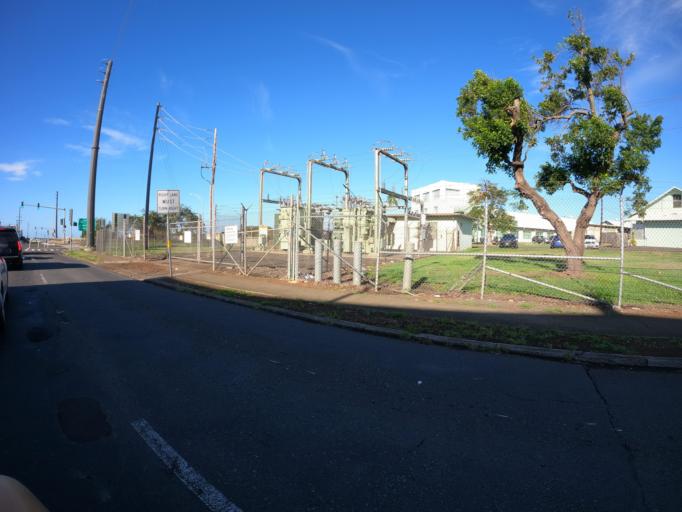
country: US
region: Hawaii
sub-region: Honolulu County
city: Honolulu
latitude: 21.3384
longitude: -157.8831
